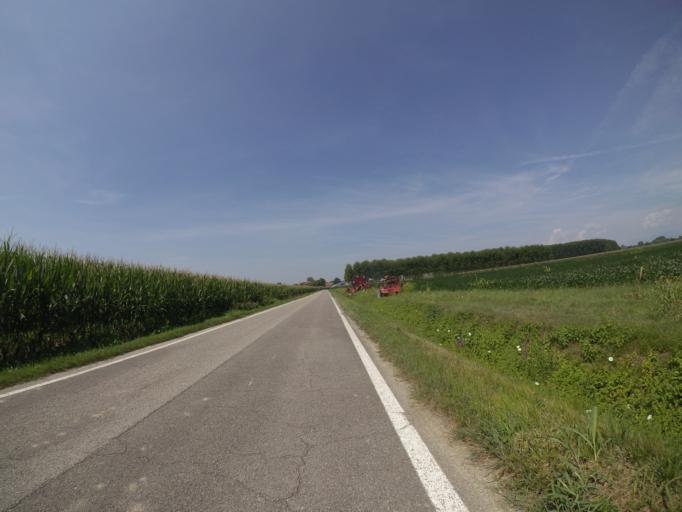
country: IT
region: Friuli Venezia Giulia
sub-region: Provincia di Udine
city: Varmo
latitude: 45.9007
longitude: 12.9726
